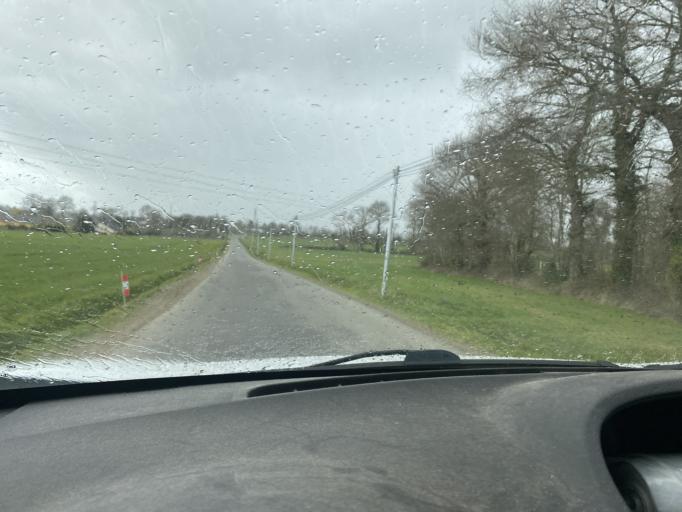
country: FR
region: Brittany
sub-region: Departement d'Ille-et-Vilaine
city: La Chapelle-des-Fougeretz
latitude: 48.1869
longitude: -1.7123
